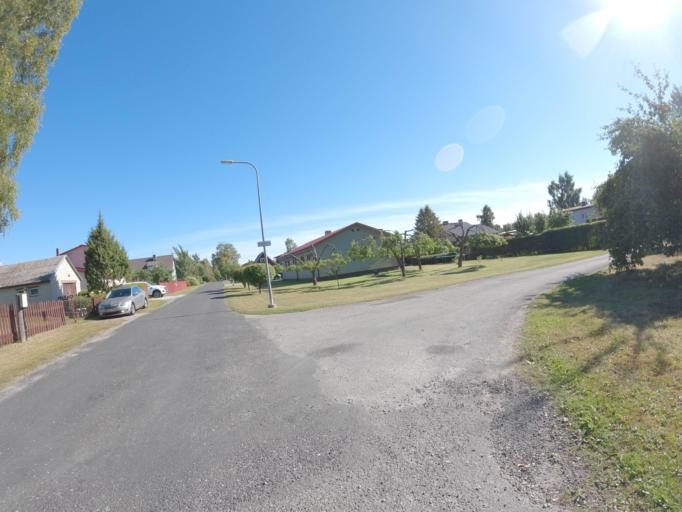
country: EE
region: Raplamaa
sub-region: Rapla vald
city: Rapla
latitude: 58.9914
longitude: 24.8197
